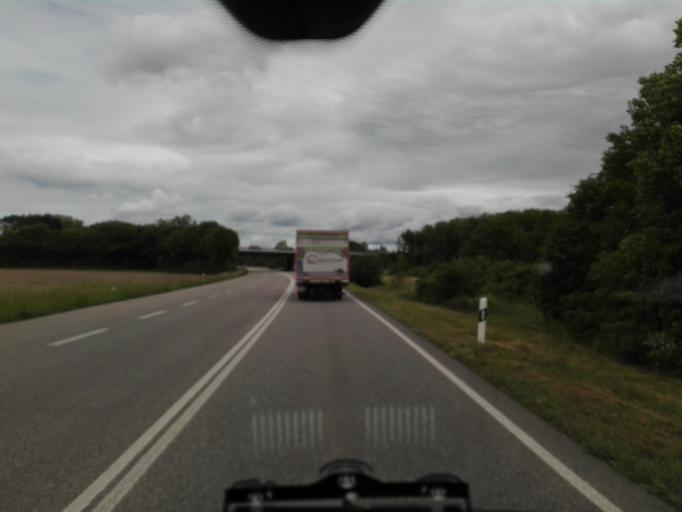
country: DE
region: Baden-Wuerttemberg
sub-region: Karlsruhe Region
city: Graben-Neudorf
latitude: 49.1823
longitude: 8.5045
